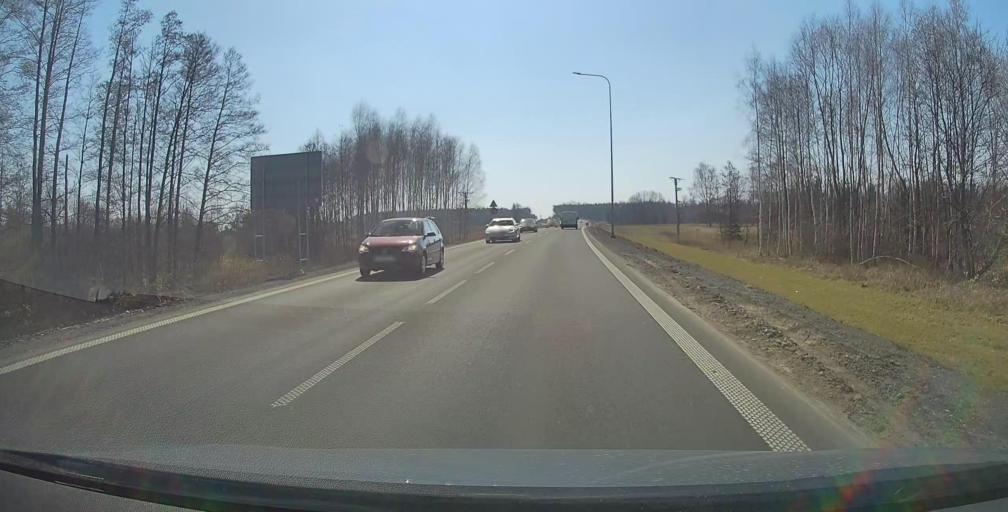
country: PL
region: Subcarpathian Voivodeship
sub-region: Powiat nizanski
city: Raclawice
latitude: 50.5159
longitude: 22.1727
